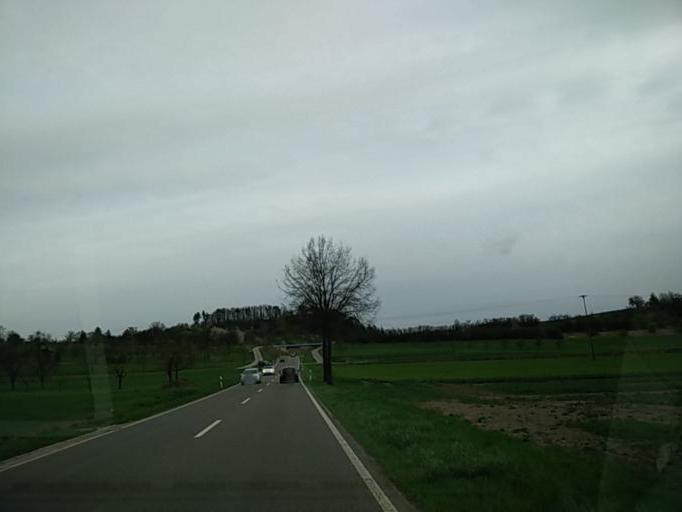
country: DE
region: Baden-Wuerttemberg
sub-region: Tuebingen Region
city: Rottenburg
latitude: 48.5423
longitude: 8.9671
